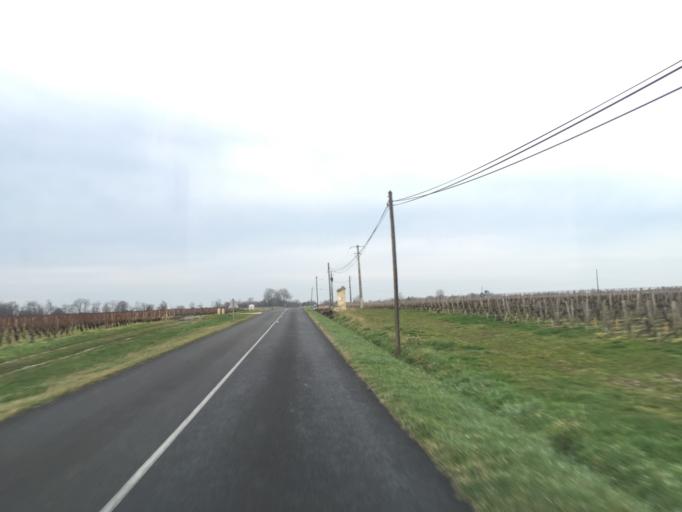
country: FR
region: Aquitaine
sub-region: Departement de la Gironde
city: Pauillac
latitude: 45.1551
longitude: -0.7720
